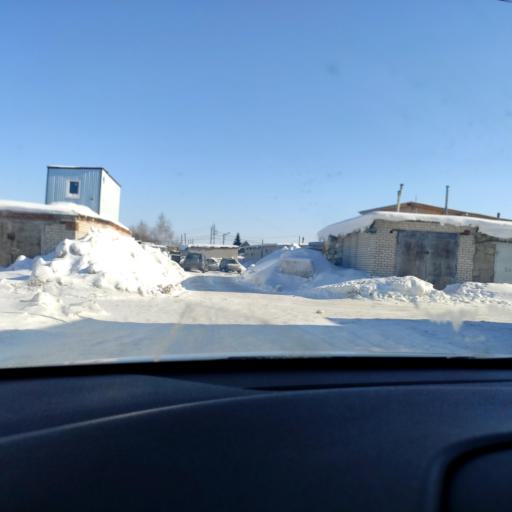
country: RU
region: Tatarstan
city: Staroye Arakchino
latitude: 55.8795
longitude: 49.0351
